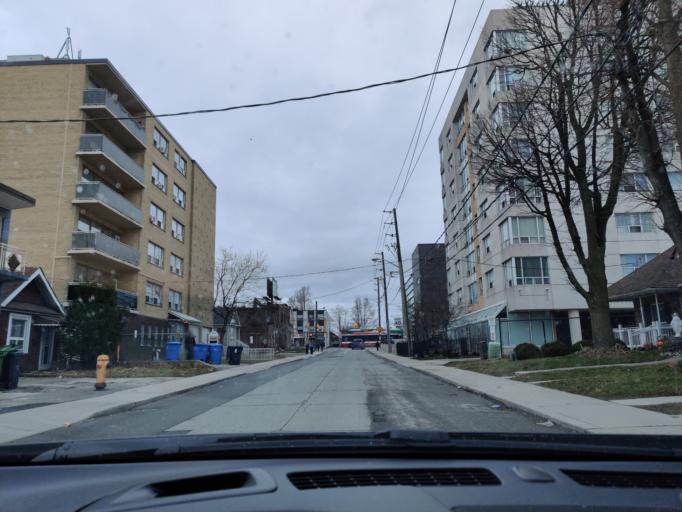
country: CA
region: Ontario
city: Toronto
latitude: 43.6953
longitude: -79.4473
